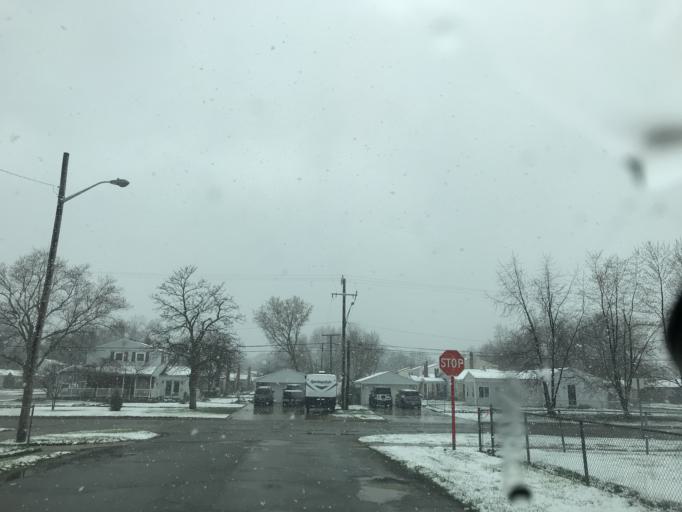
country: US
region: Michigan
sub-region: Wayne County
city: Taylor
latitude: 42.2308
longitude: -83.2489
